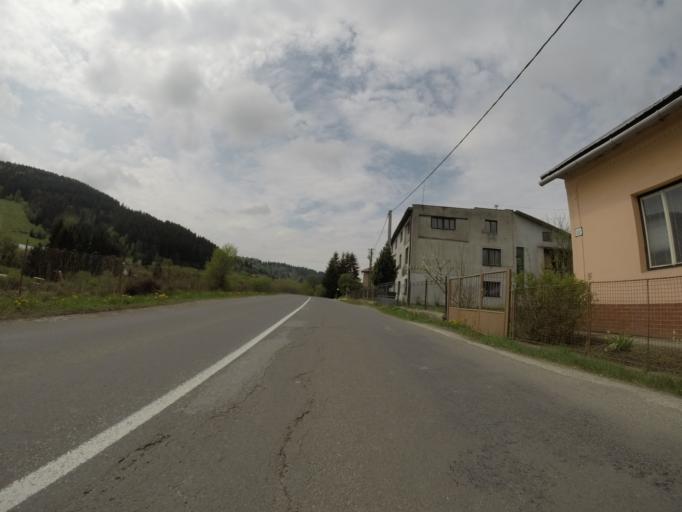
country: SK
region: Banskobystricky
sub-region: Okres Banska Bystrica
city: Brezno
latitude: 48.8263
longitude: 19.7414
